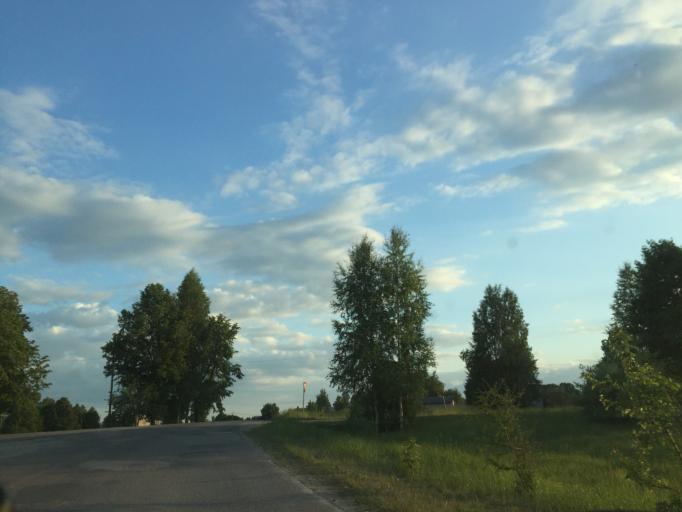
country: LV
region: Sigulda
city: Sigulda
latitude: 57.1106
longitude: 24.9388
